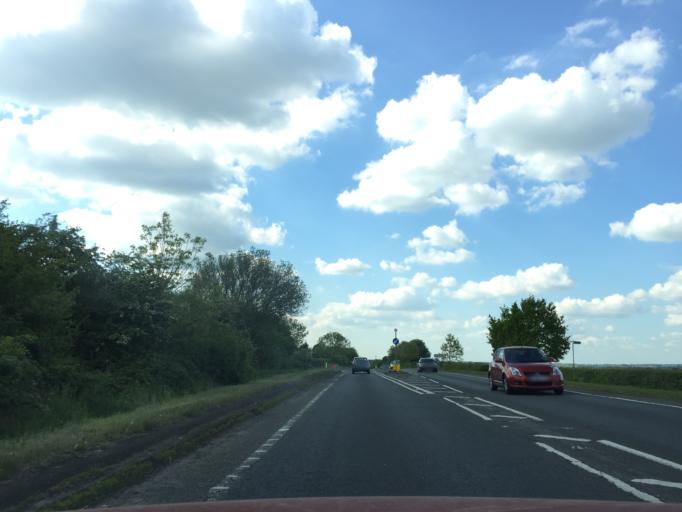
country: GB
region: England
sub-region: Milton Keynes
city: Castlethorpe
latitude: 52.0924
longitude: -0.8753
